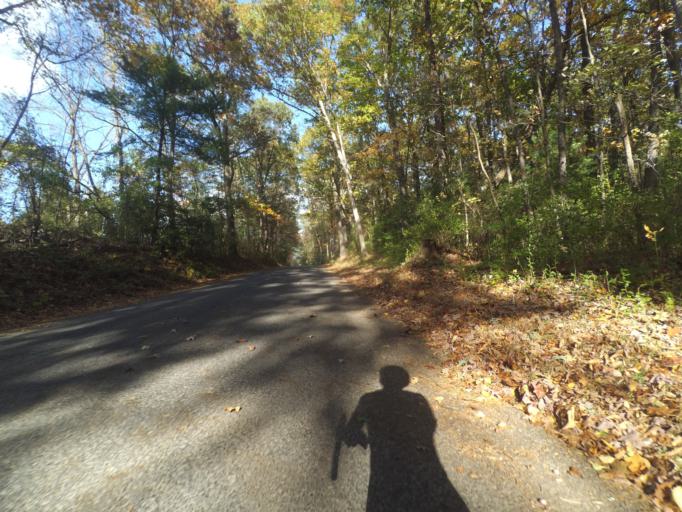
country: US
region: Pennsylvania
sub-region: Centre County
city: Houserville
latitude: 40.8589
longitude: -77.8253
